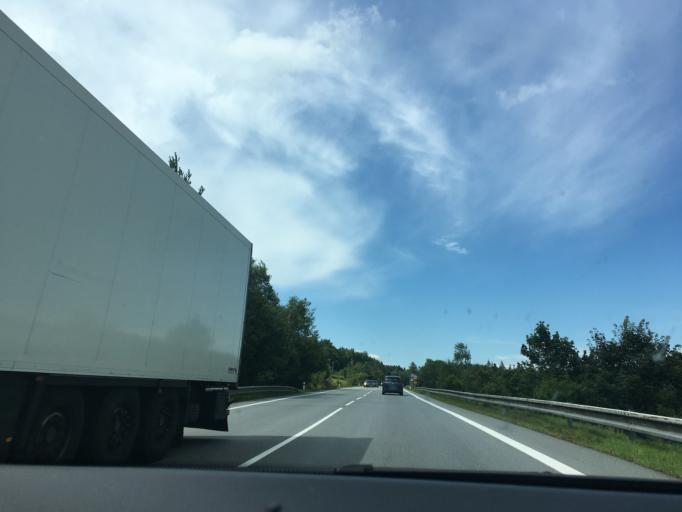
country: PL
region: Subcarpathian Voivodeship
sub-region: Powiat krosnienski
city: Jasliska
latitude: 49.4056
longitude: 21.7032
